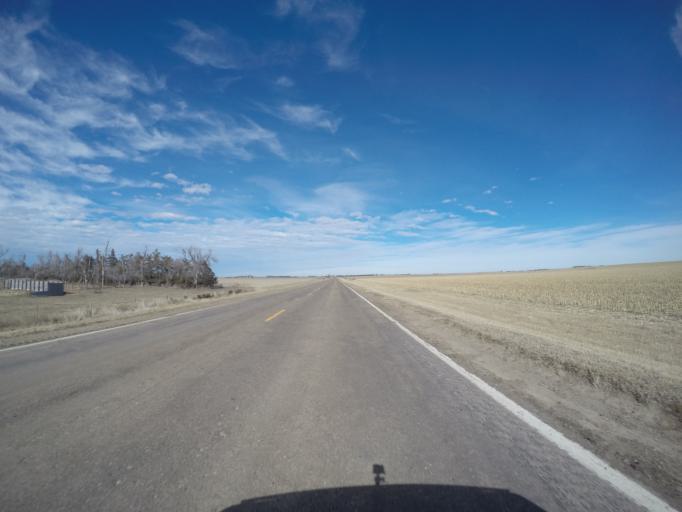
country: US
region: Nebraska
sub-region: Franklin County
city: Franklin
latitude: 40.1765
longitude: -98.9526
